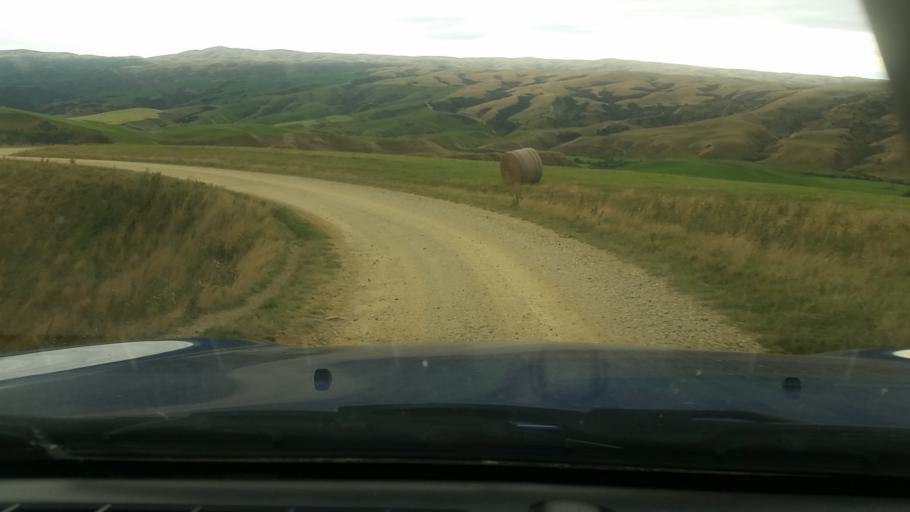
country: NZ
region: Otago
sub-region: Clutha District
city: Balclutha
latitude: -45.7172
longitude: 169.5335
